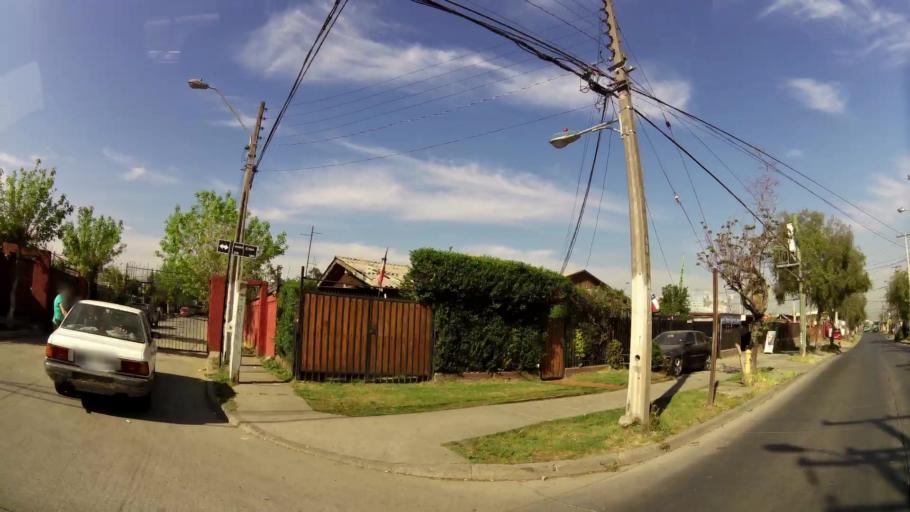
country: CL
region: Santiago Metropolitan
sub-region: Provincia de Santiago
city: La Pintana
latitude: -33.5623
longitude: -70.6014
